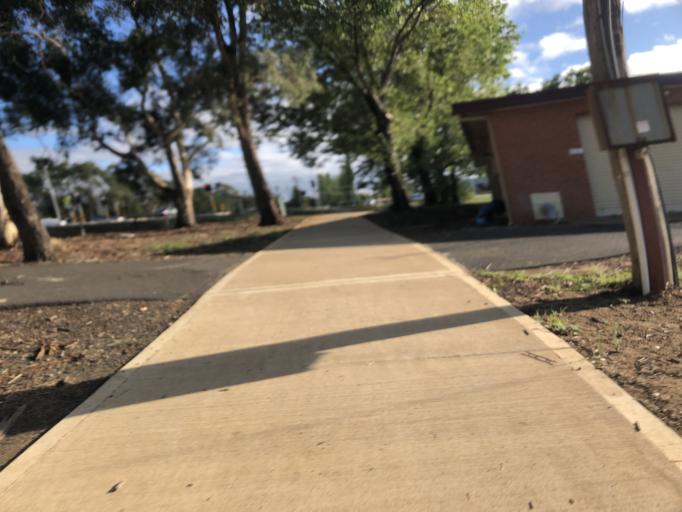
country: AU
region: New South Wales
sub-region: Orange Municipality
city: Orange
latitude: -33.3073
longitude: 149.0985
